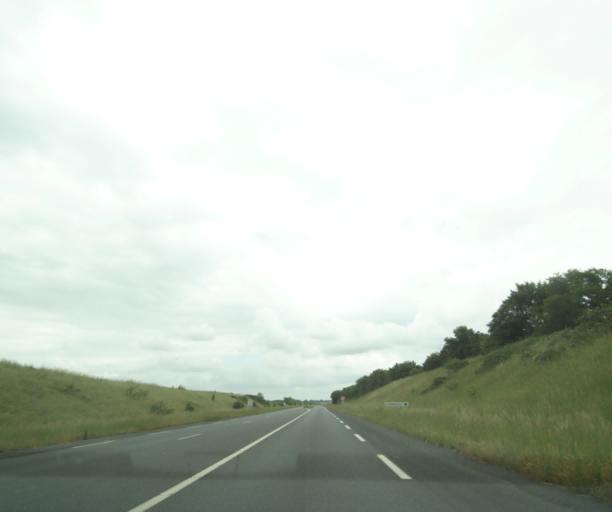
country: FR
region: Poitou-Charentes
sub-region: Departement des Deux-Sevres
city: Saint-Varent
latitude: 46.8874
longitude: -0.1942
